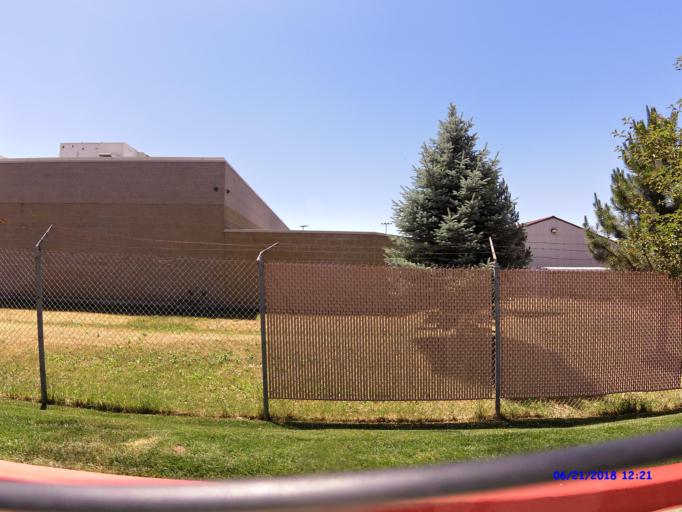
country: US
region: Utah
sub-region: Weber County
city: Harrisville
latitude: 41.2829
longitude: -111.9981
